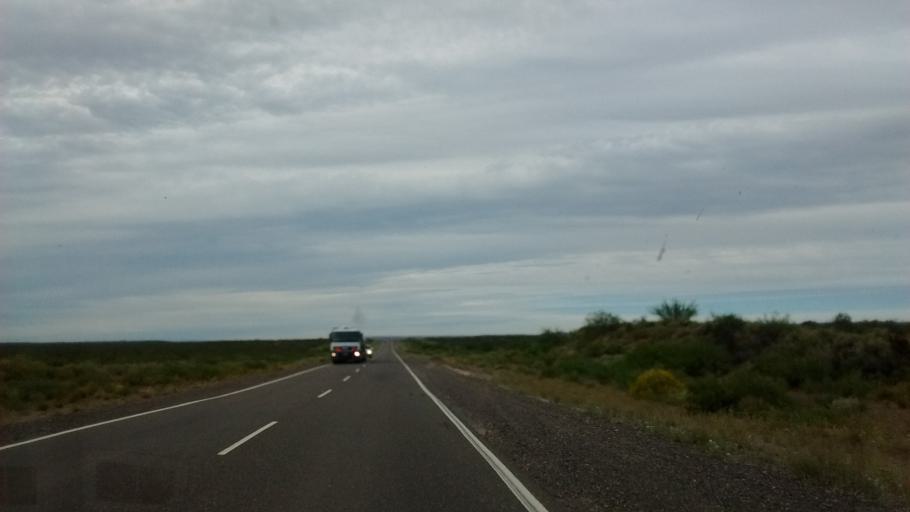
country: AR
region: Rio Negro
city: Catriel
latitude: -38.0927
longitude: -67.9267
